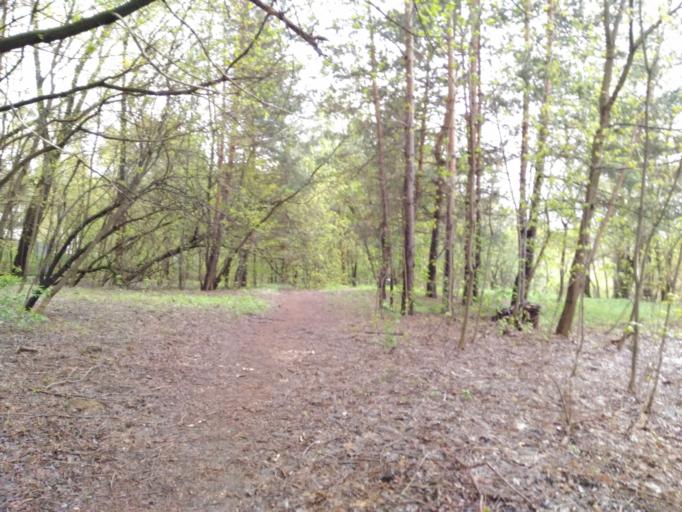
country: RU
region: Moscow
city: Strogino
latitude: 55.7869
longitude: 37.4092
